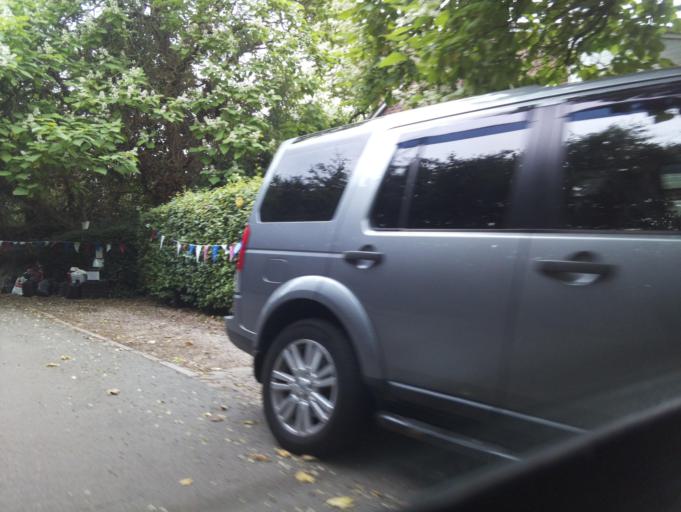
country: GB
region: England
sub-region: Derbyshire
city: Long Eaton
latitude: 52.9152
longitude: -1.3199
